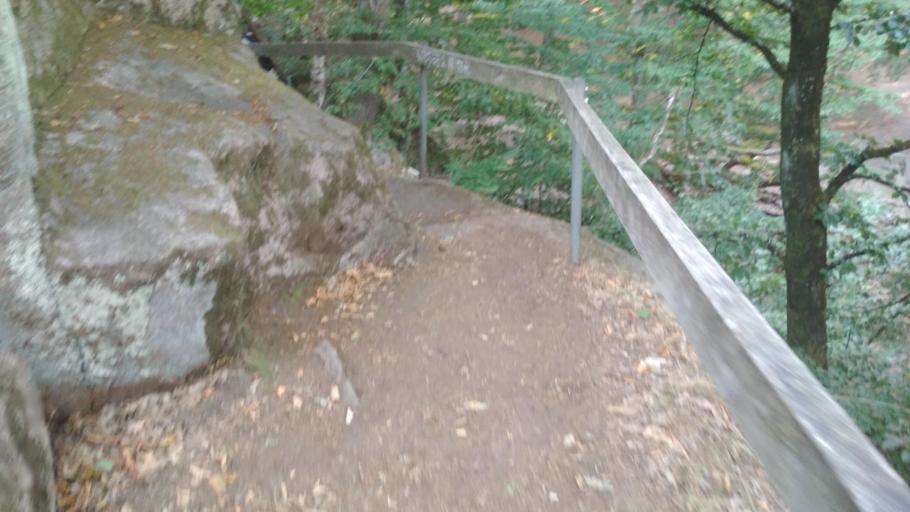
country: DK
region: Capital Region
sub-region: Bornholm Kommune
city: Akirkeby
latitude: 55.1097
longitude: 14.9005
